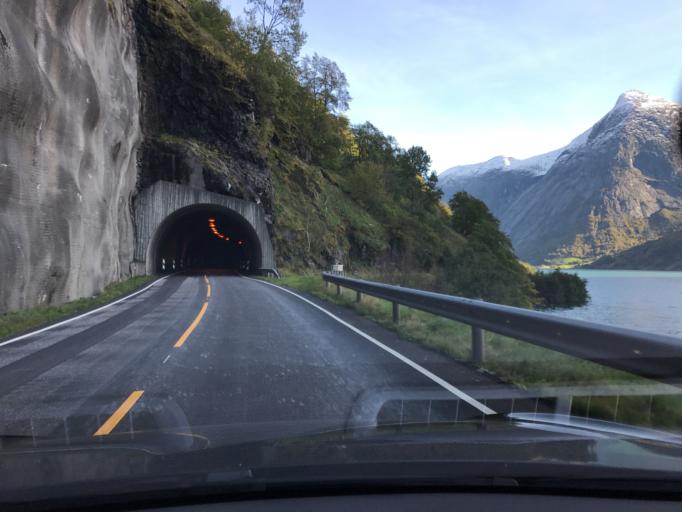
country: NO
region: Sogn og Fjordane
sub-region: Jolster
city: Skei
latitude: 61.5395
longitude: 6.5445
